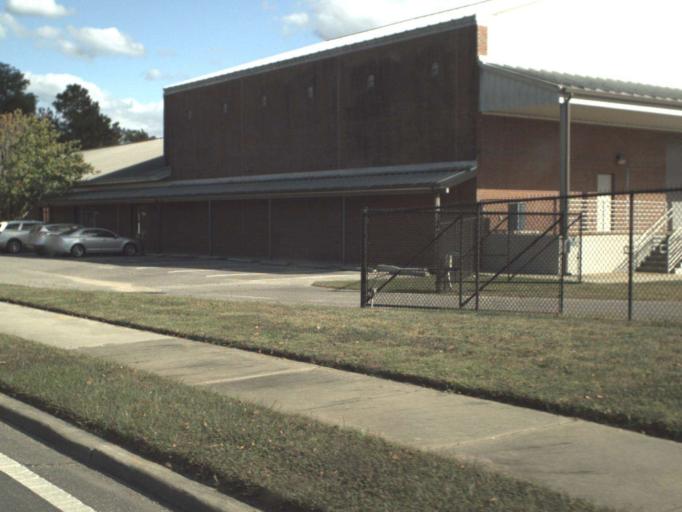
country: US
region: Florida
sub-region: Washington County
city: Chipley
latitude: 30.7805
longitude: -85.5267
